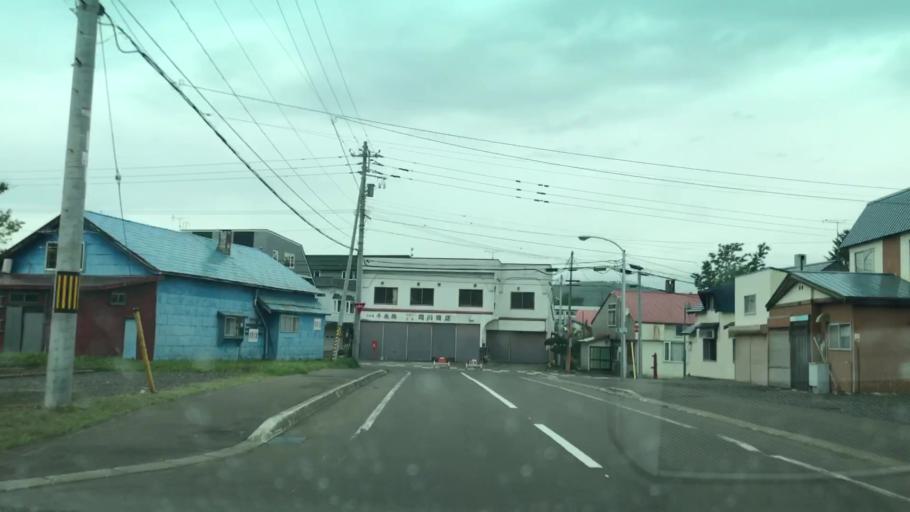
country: JP
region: Hokkaido
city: Niseko Town
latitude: 42.8030
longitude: 140.5268
